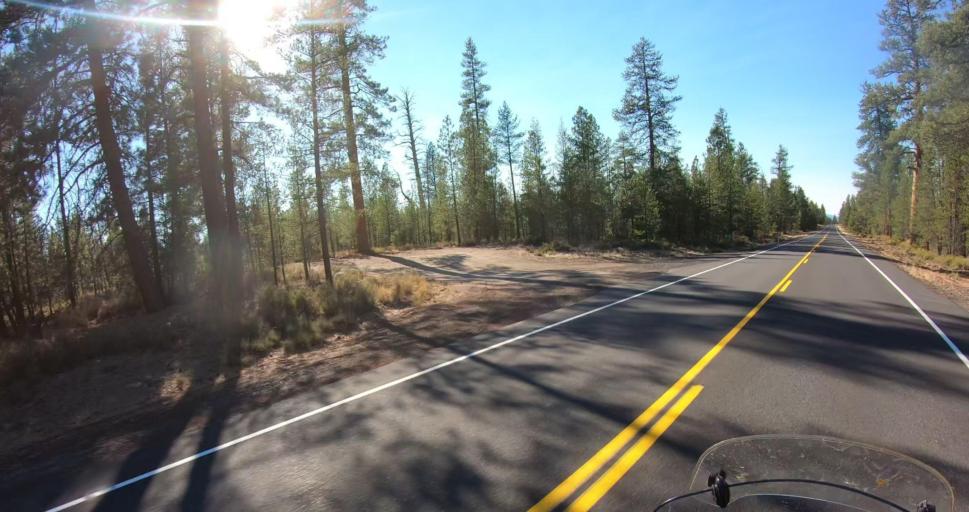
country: US
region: Oregon
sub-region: Deschutes County
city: La Pine
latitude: 43.4872
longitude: -121.4312
